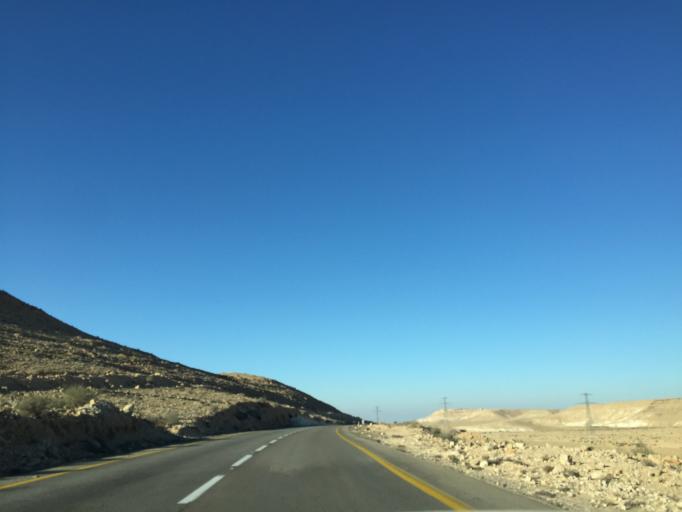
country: IL
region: Southern District
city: Midreshet Ben-Gurion
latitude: 30.7634
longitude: 34.7722
